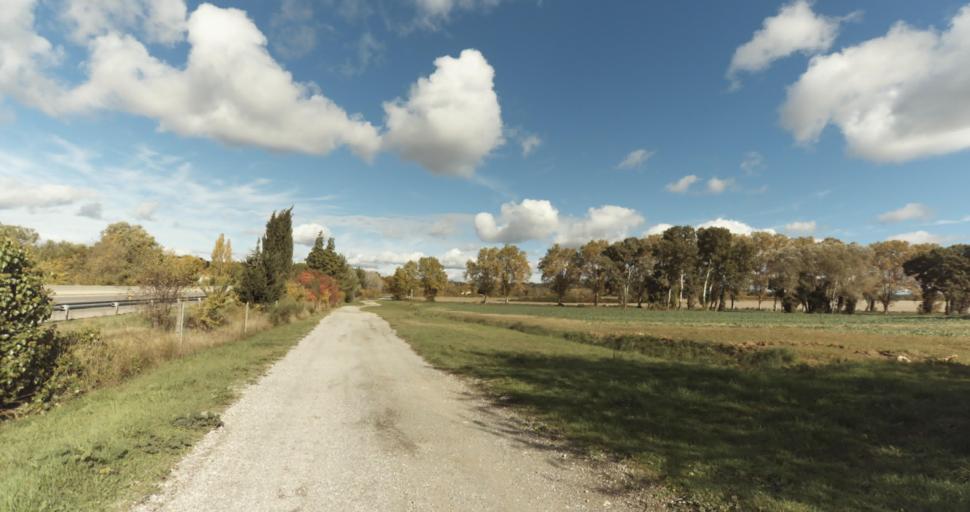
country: FR
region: Provence-Alpes-Cote d'Azur
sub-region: Departement des Bouches-du-Rhone
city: Venelles
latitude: 43.5826
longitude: 5.4765
